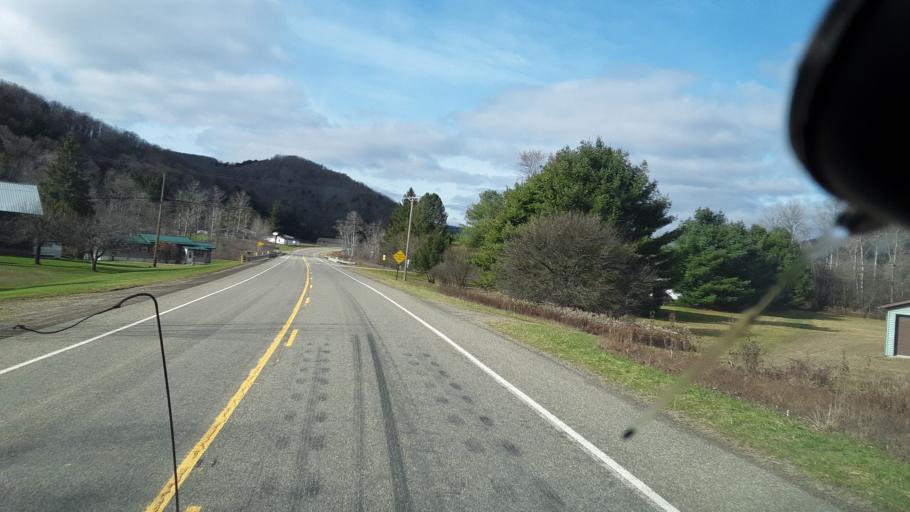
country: US
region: Pennsylvania
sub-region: Potter County
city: Galeton
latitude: 41.7815
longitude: -77.7350
